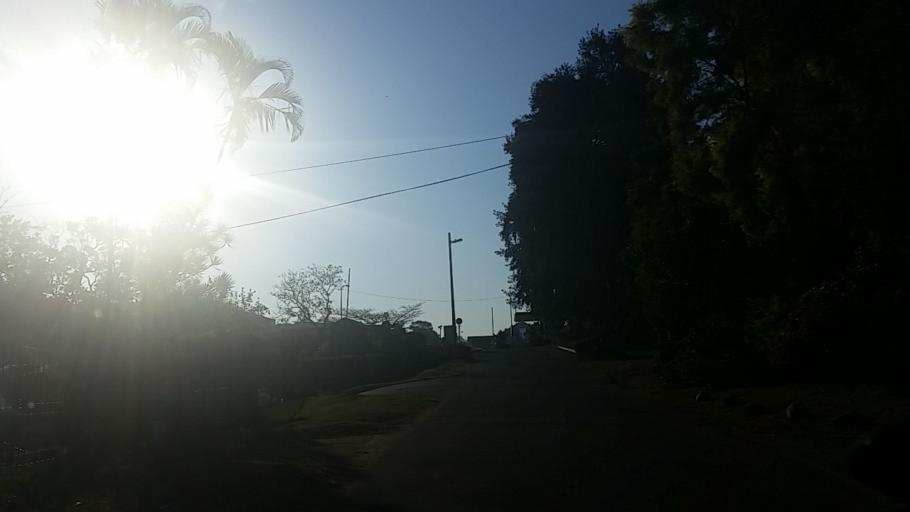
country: ZA
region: KwaZulu-Natal
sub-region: eThekwini Metropolitan Municipality
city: Berea
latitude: -29.8367
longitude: 30.9149
